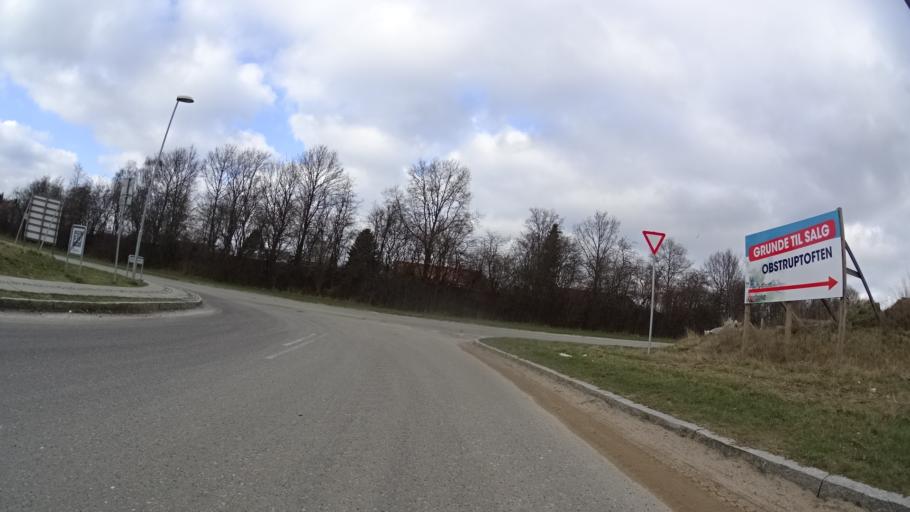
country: DK
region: Central Jutland
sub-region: Arhus Kommune
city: Marslet
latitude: 56.0841
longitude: 10.1476
